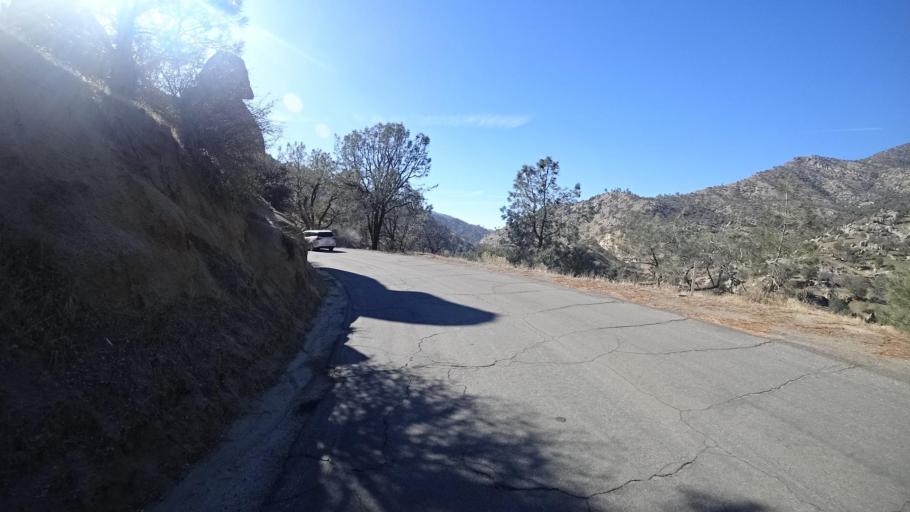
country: US
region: California
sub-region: Kern County
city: Bodfish
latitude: 35.5769
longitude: -118.5576
